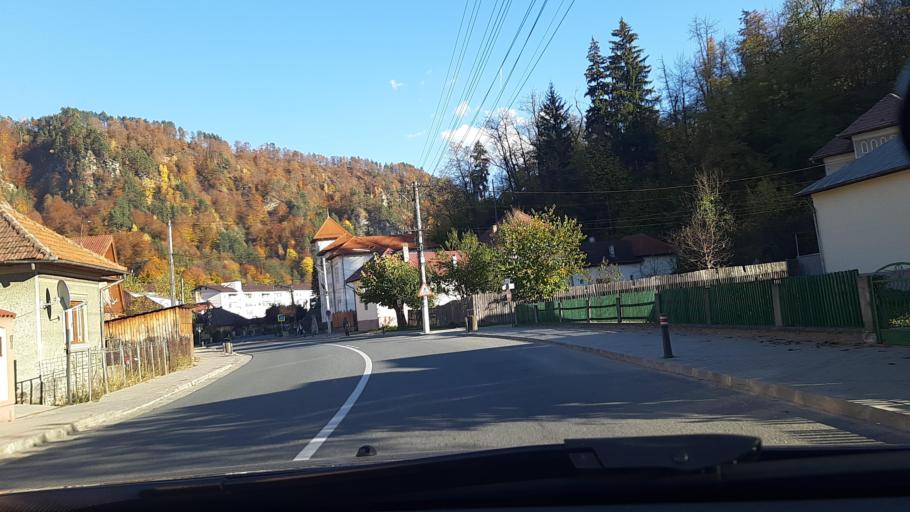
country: RO
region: Valcea
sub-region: Comuna Brezoi
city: Brezoi
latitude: 45.3439
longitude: 24.2424
